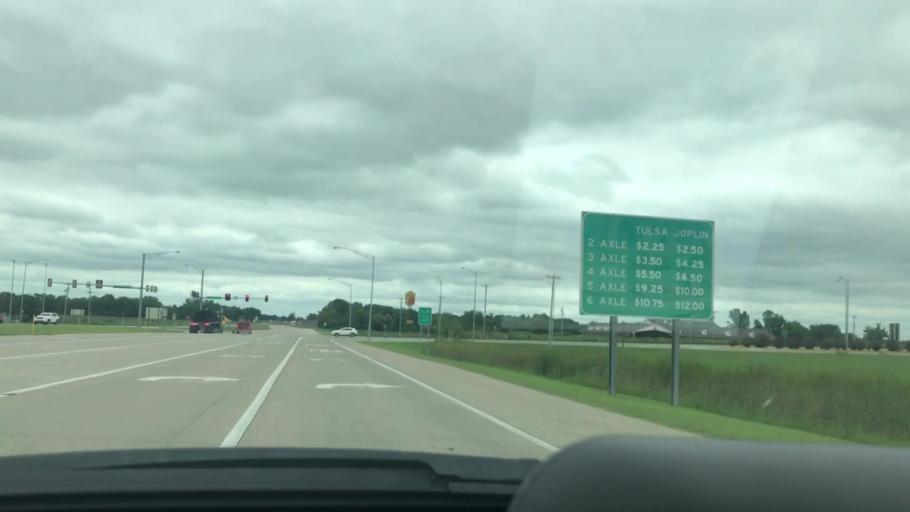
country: US
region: Oklahoma
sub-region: Craig County
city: Vinita
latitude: 36.5661
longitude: -95.2200
